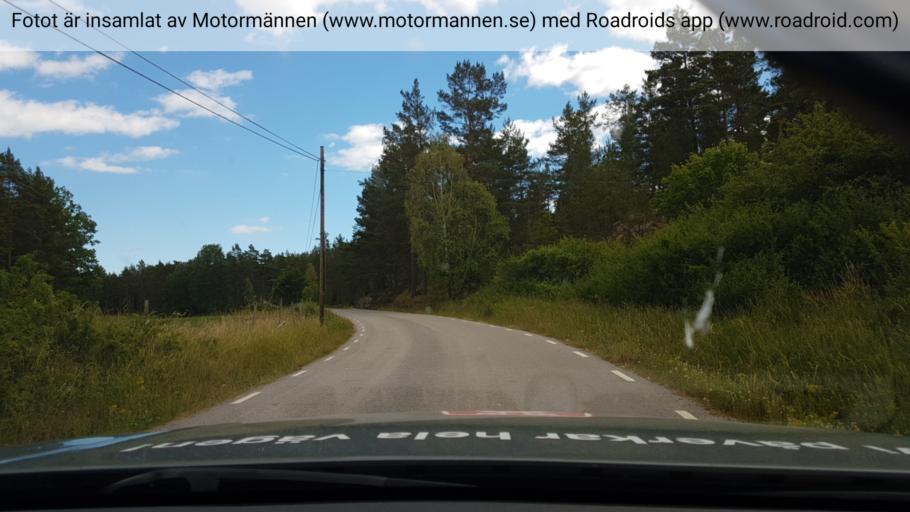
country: SE
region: Kalmar
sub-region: Vasterviks Kommun
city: Vaestervik
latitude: 57.9191
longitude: 16.6840
